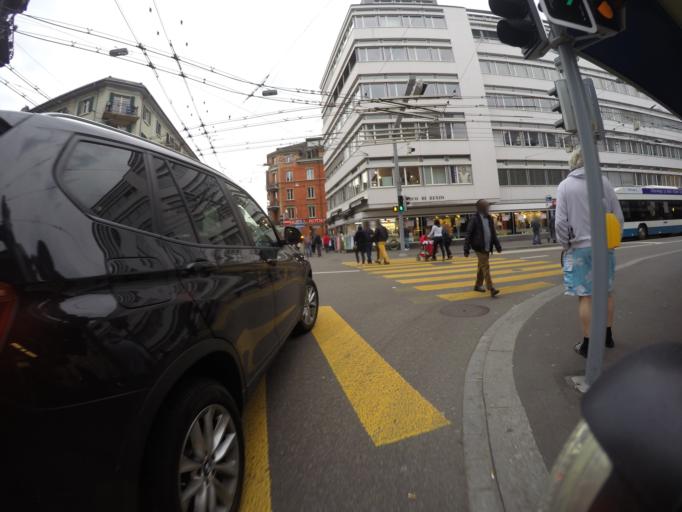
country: CH
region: Zurich
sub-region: Bezirk Zuerich
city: Zuerich (Kreis 4) / Langstrasse
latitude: 47.3798
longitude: 8.5277
